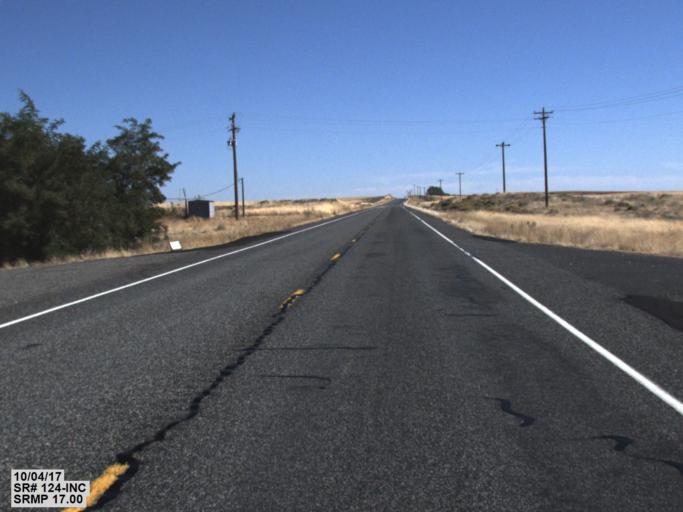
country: US
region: Washington
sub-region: Walla Walla County
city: Burbank
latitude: 46.2976
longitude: -118.7009
